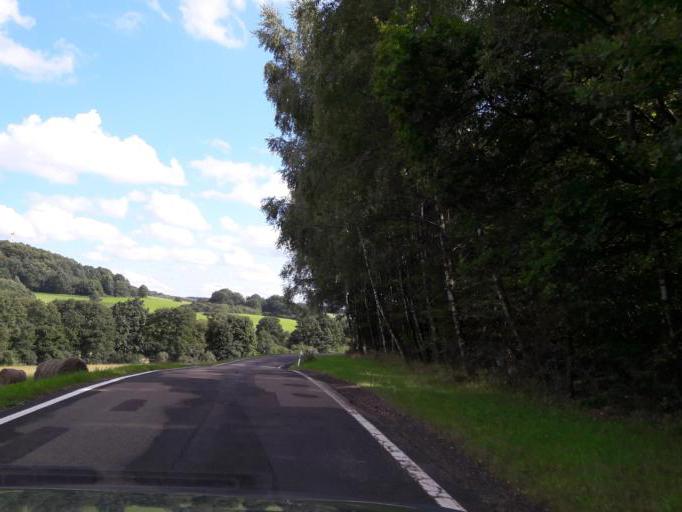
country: DE
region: Rheinland-Pfalz
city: Gimbweiler
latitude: 49.5789
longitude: 7.1843
